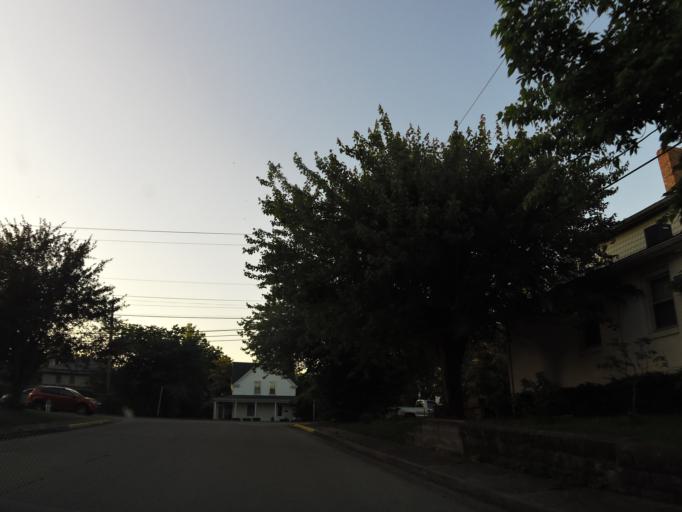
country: US
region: Kentucky
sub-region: Madison County
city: Berea
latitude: 37.5677
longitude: -84.3017
